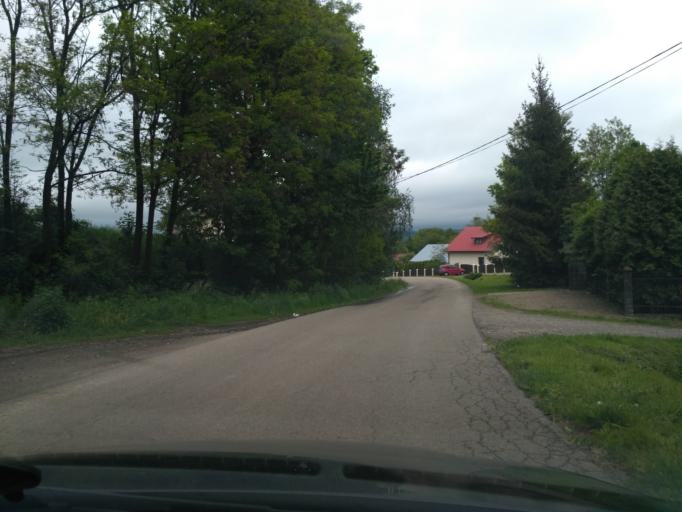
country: PL
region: Subcarpathian Voivodeship
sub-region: Powiat jasielski
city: Brzyska
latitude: 49.8226
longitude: 21.3636
